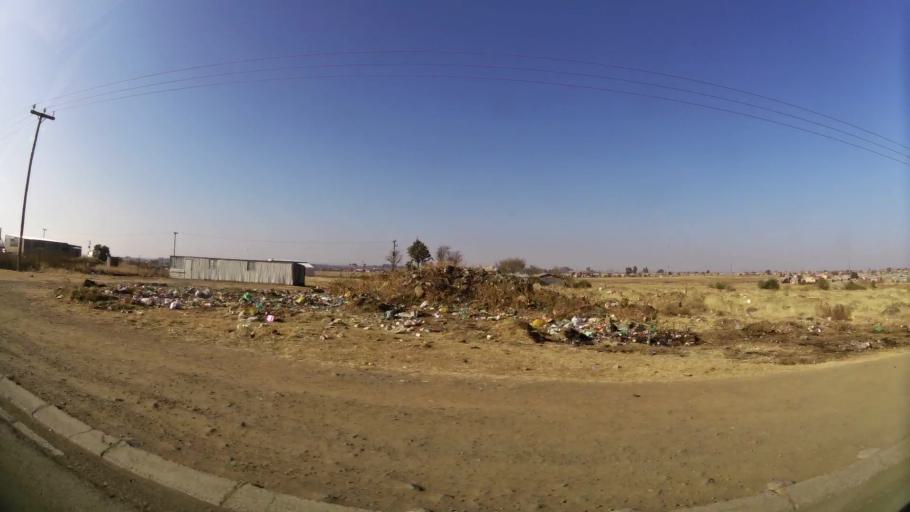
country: ZA
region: Orange Free State
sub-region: Mangaung Metropolitan Municipality
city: Bloemfontein
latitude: -29.1960
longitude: 26.2658
